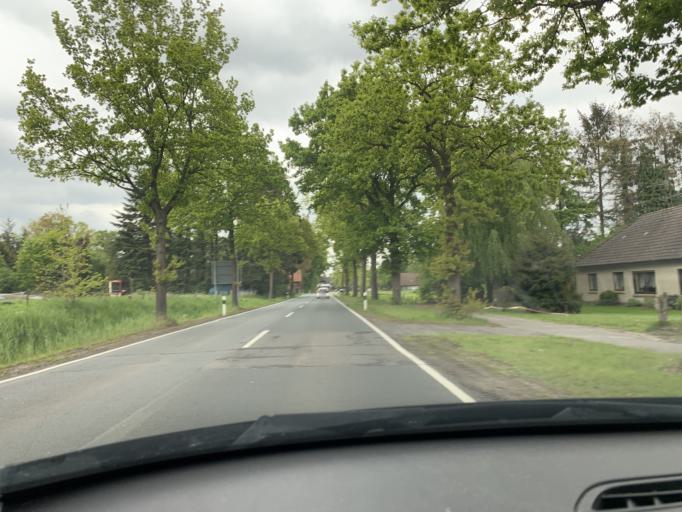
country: DE
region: Lower Saxony
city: Bad Zwischenahn
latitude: 53.2159
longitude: 8.0092
